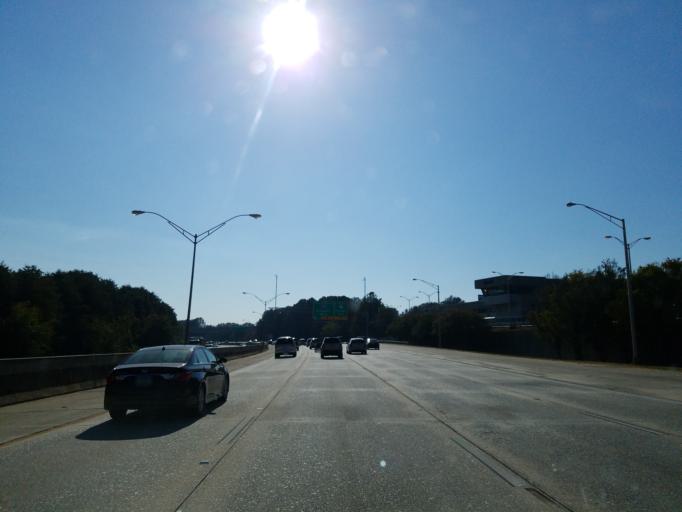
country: US
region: Georgia
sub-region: Fulton County
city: College Park
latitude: 33.6399
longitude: -84.4551
